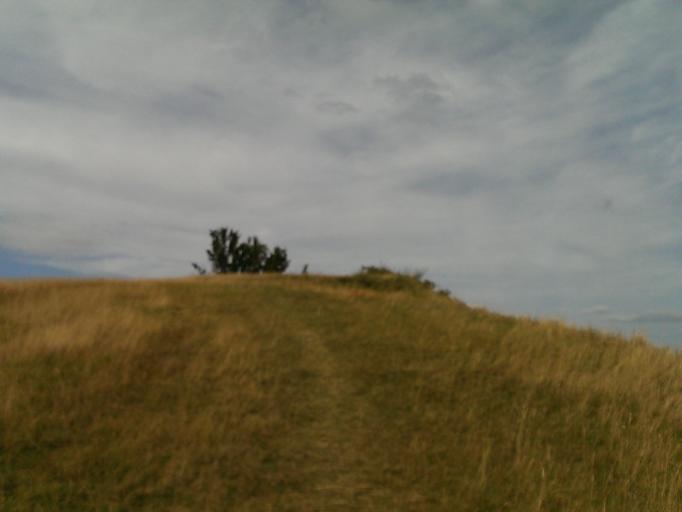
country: DK
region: Central Jutland
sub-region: Syddjurs Kommune
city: Ebeltoft
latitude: 56.1053
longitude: 10.5482
